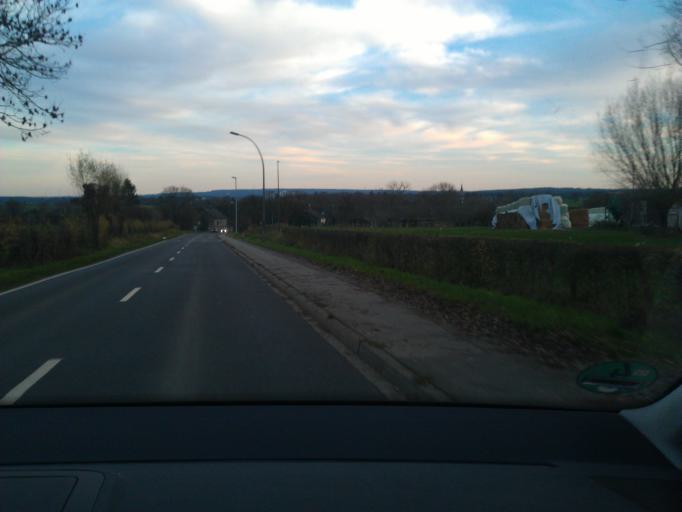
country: BE
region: Wallonia
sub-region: Province de Liege
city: Raeren
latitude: 50.7181
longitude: 6.1623
